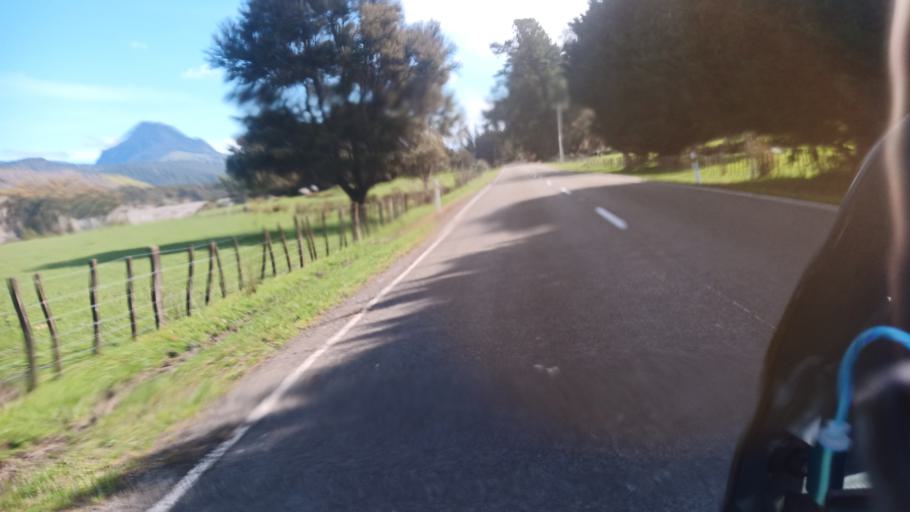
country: NZ
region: Gisborne
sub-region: Gisborne District
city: Gisborne
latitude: -37.8656
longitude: 178.1970
